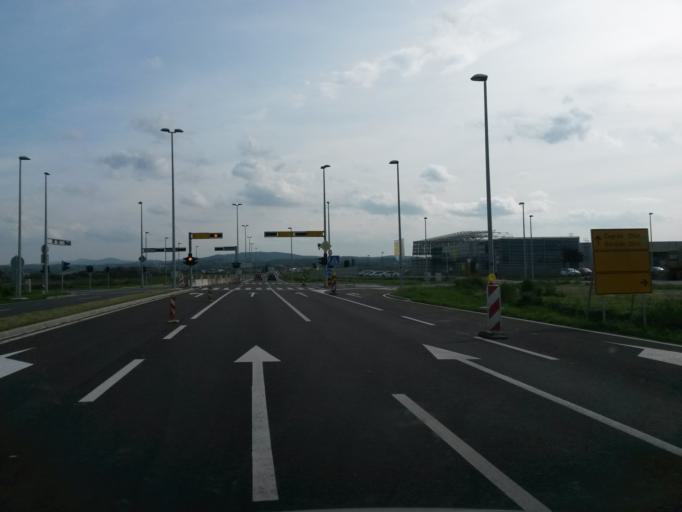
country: HR
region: Varazdinska
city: Varazdin
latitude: 46.2740
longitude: 16.3615
